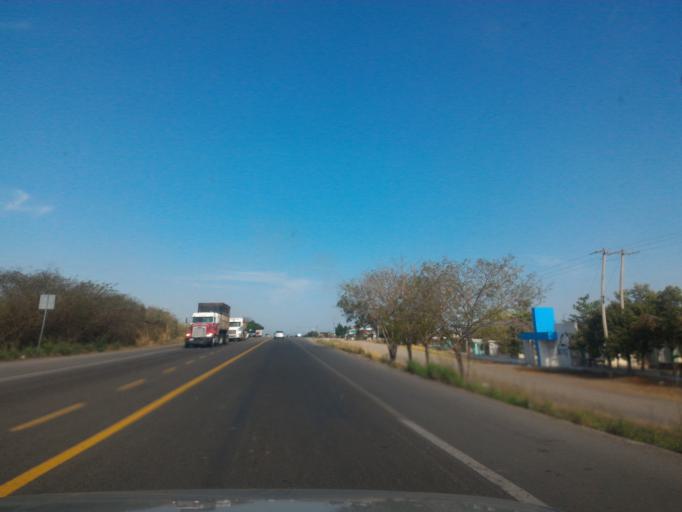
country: MX
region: Michoacan
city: Coahuayana Viejo
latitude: 18.7595
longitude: -103.7278
